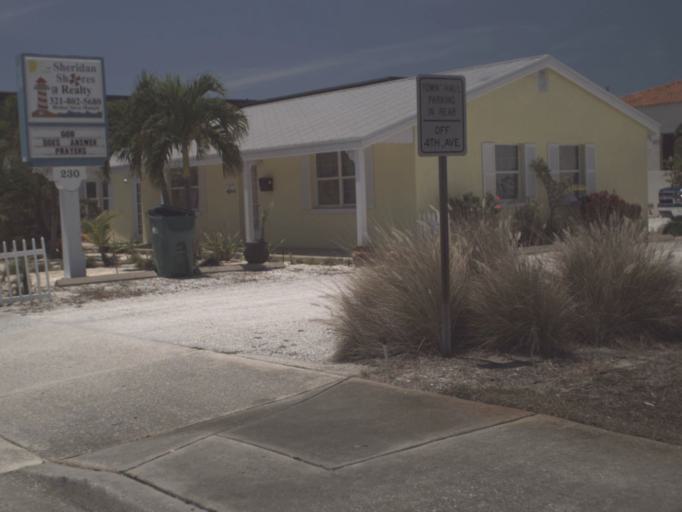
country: US
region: Florida
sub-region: Brevard County
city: Indialantic
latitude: 28.0907
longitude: -80.5700
